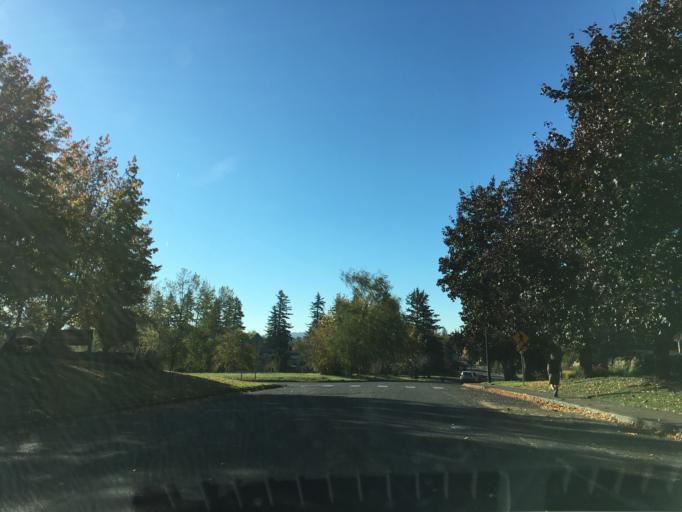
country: US
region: Oregon
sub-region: Multnomah County
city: Wood Village
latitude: 45.5160
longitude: -122.4092
